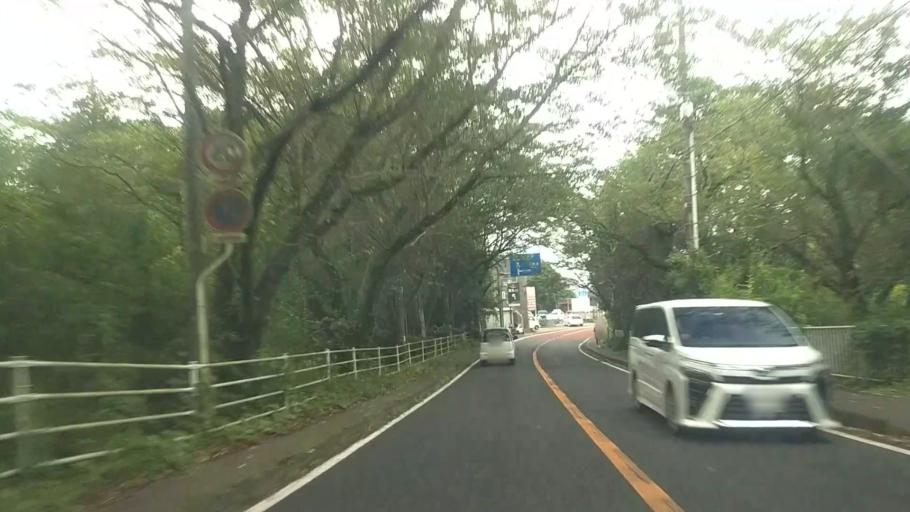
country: JP
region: Chiba
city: Kisarazu
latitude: 35.2998
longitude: 140.0748
